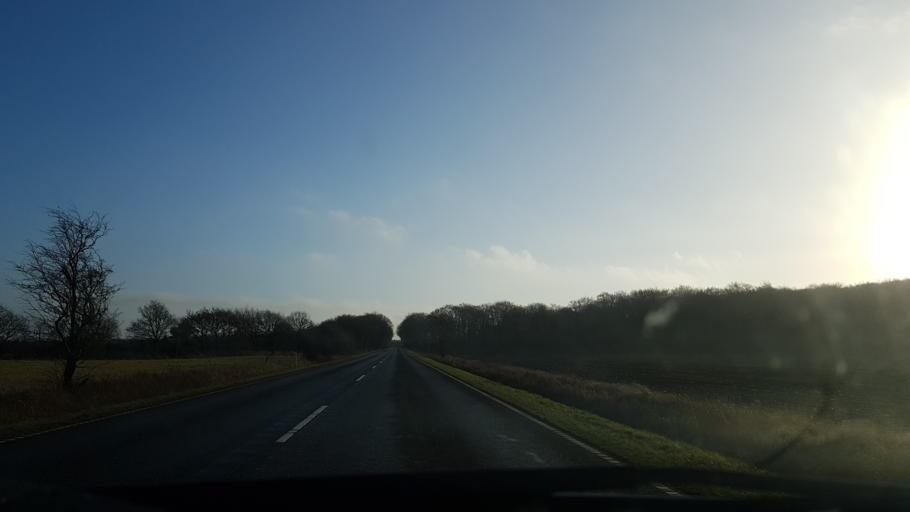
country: DK
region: South Denmark
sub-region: Tonder Kommune
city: Toftlund
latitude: 55.2255
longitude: 9.1743
